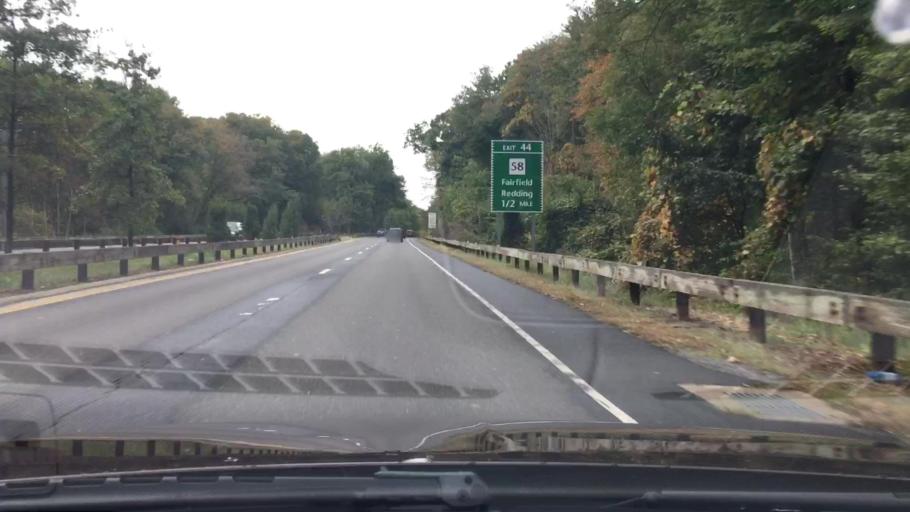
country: US
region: Connecticut
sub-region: Fairfield County
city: Fairfield
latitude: 41.2101
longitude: -73.2632
